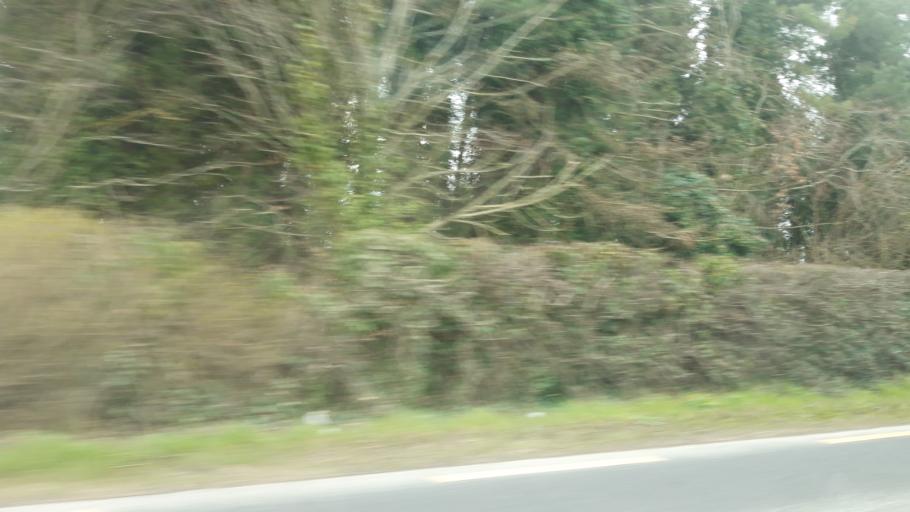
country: IE
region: Leinster
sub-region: Kildare
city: Clane
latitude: 53.3013
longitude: -6.6712
